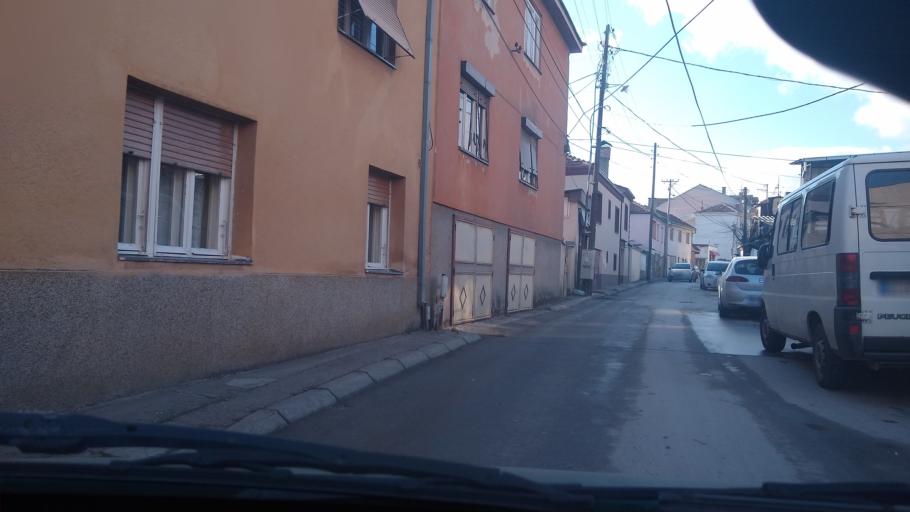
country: MK
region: Bitola
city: Bitola
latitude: 41.0265
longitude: 21.3293
